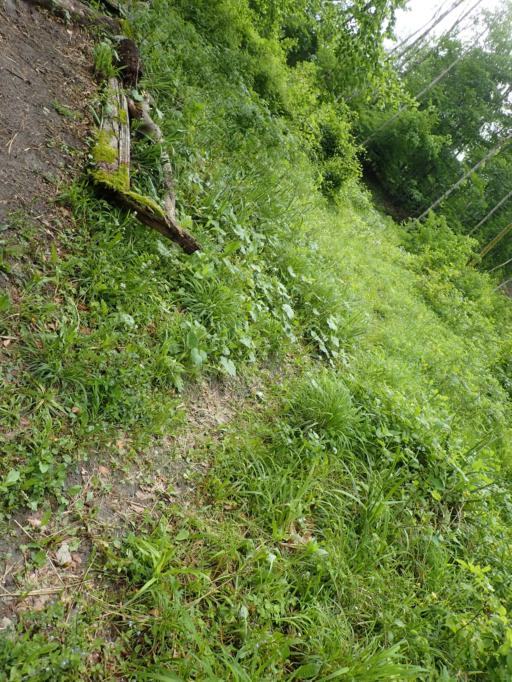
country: DE
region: Bavaria
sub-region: Upper Bavaria
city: Marktschellenberg
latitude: 47.7082
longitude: 13.0601
